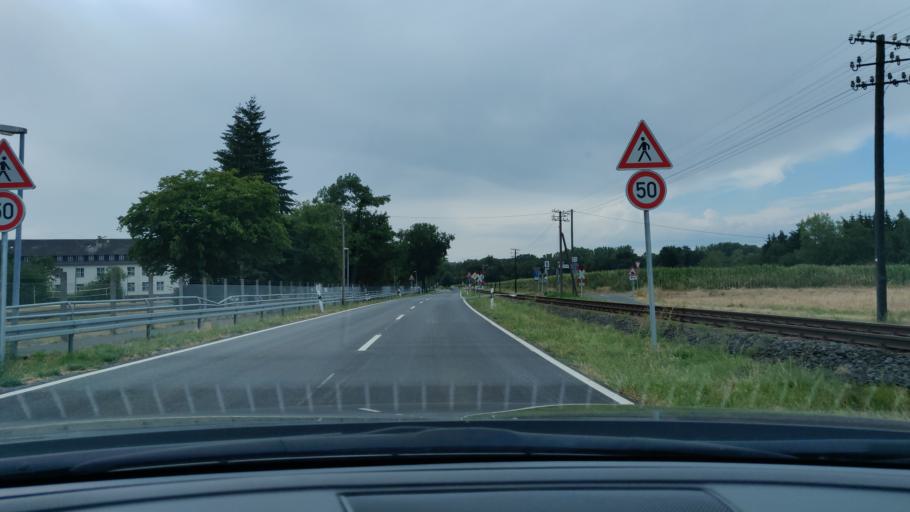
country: DE
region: Hesse
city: Fritzlar
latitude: 51.1227
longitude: 9.2947
